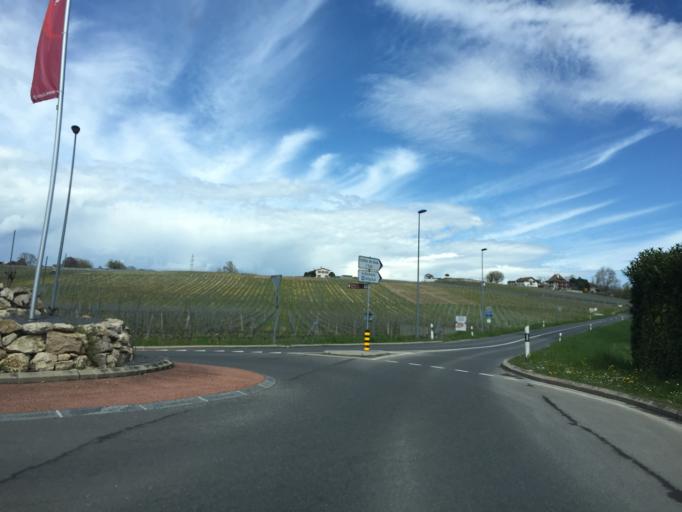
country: CH
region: Vaud
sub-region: Morges District
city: Morges
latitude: 46.5183
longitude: 6.4885
